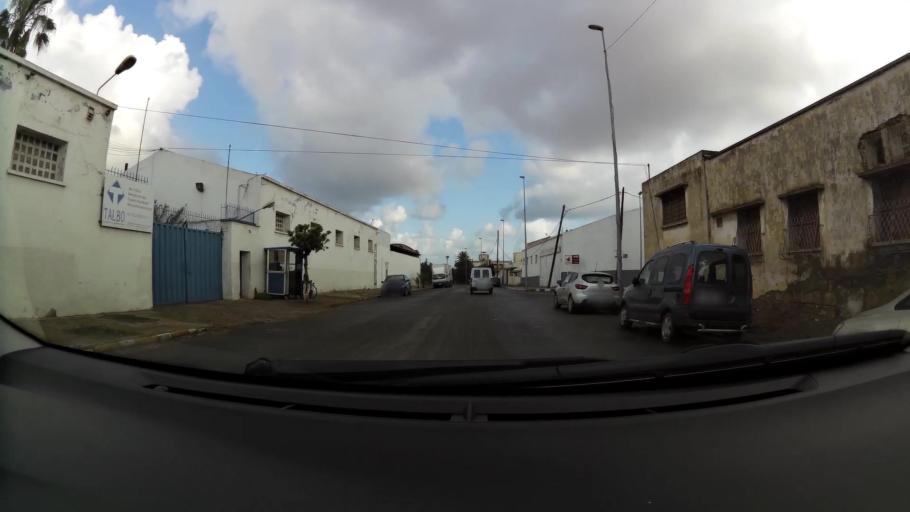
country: MA
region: Grand Casablanca
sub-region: Mediouna
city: Tit Mellil
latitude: 33.5913
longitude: -7.5439
